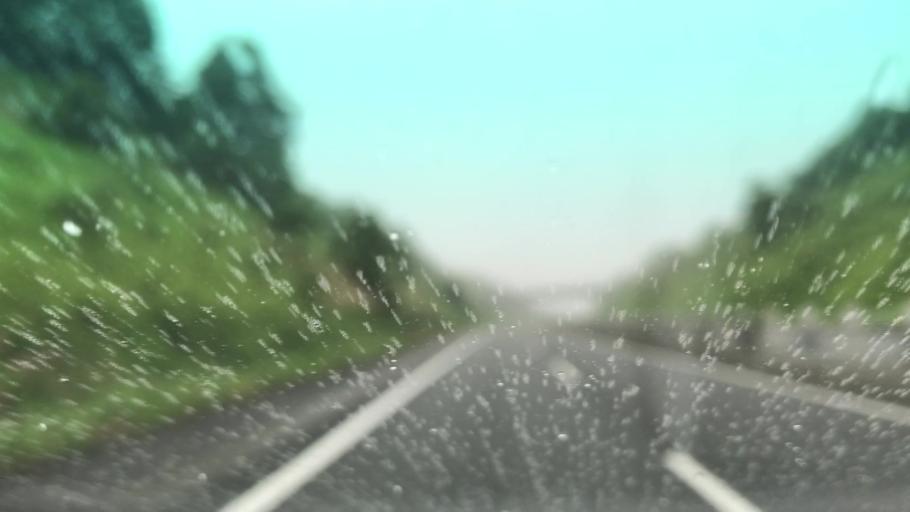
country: JP
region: Hokkaido
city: Tomakomai
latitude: 42.6220
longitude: 141.4788
